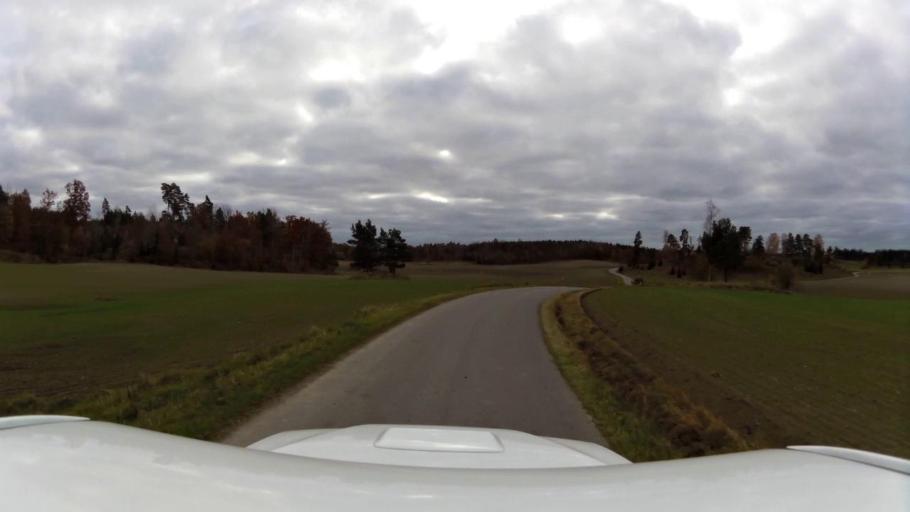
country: SE
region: OEstergoetland
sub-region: Linkopings Kommun
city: Linghem
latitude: 58.3877
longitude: 15.8362
